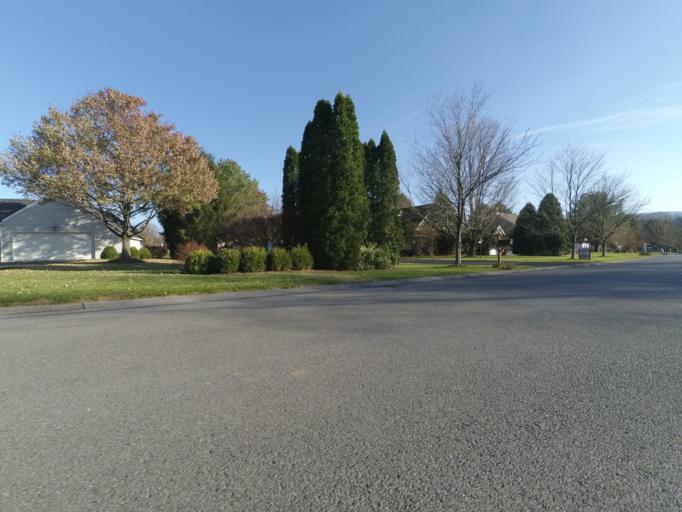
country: US
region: Pennsylvania
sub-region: Centre County
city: Lemont
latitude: 40.7939
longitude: -77.8275
